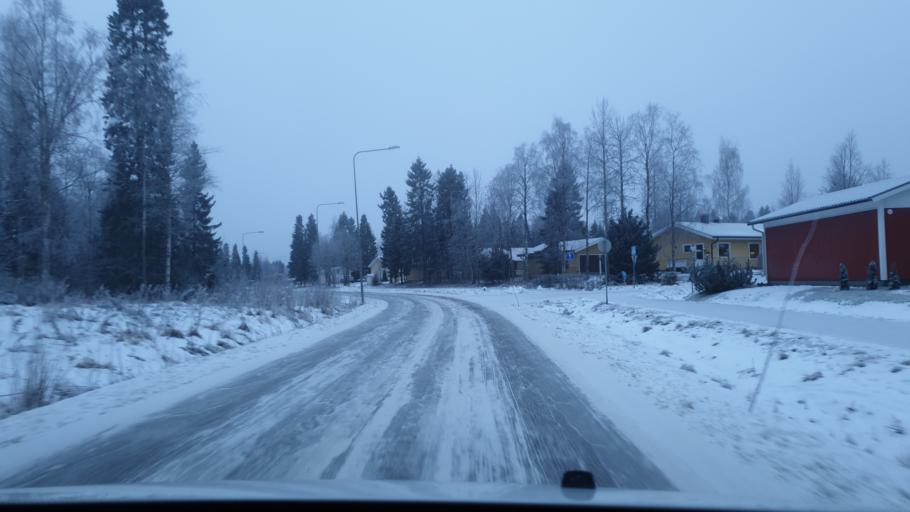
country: FI
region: Lapland
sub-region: Kemi-Tornio
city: Kemi
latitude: 65.7416
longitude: 24.6089
